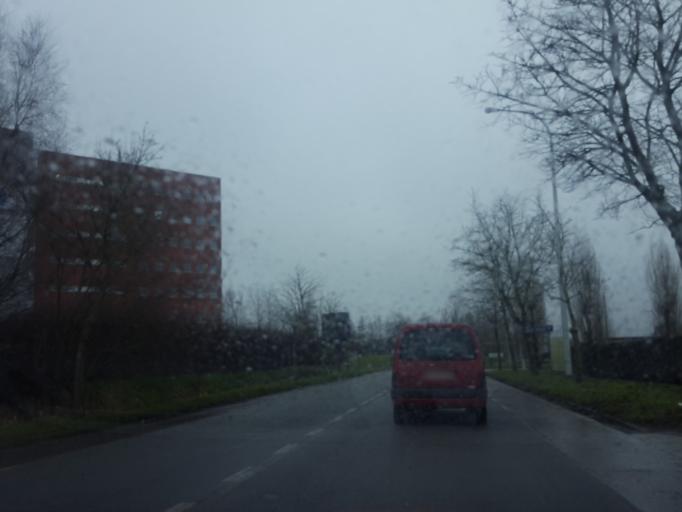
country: BE
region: Flanders
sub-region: Provincie West-Vlaanderen
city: Ieper
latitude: 50.8699
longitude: 2.8881
